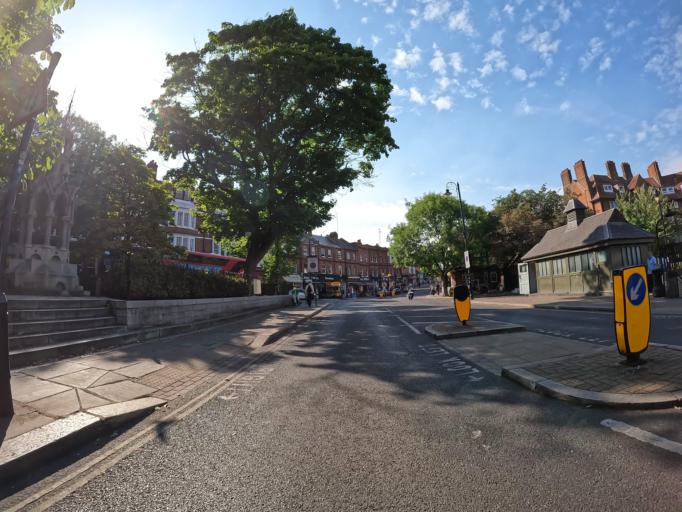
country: GB
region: England
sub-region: Greater London
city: Hendon
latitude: 51.6109
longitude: -0.2188
